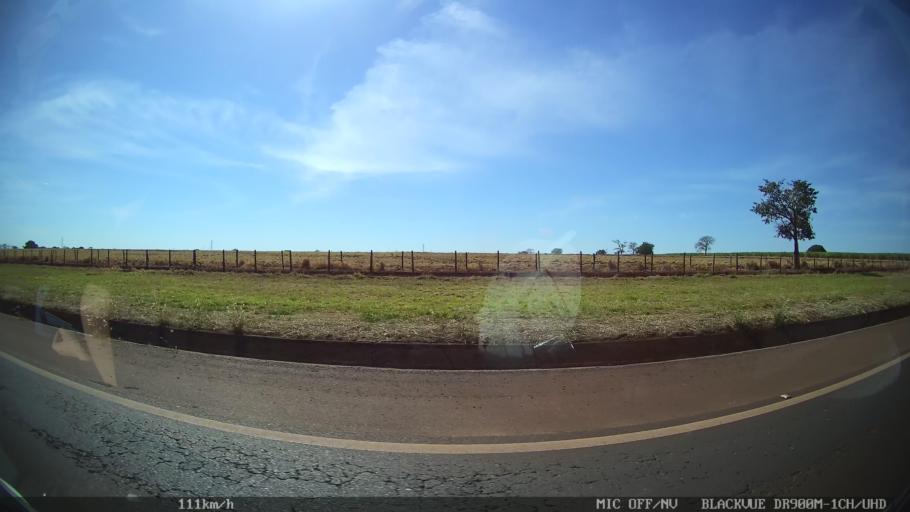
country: BR
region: Sao Paulo
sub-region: Ipua
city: Ipua
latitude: -20.4763
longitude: -48.0916
